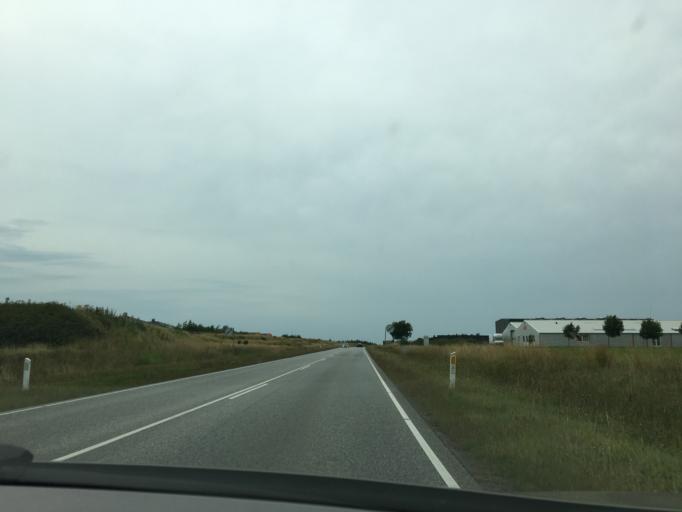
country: DK
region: Central Jutland
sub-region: Ringkobing-Skjern Kommune
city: Ringkobing
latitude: 56.0908
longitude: 8.2780
